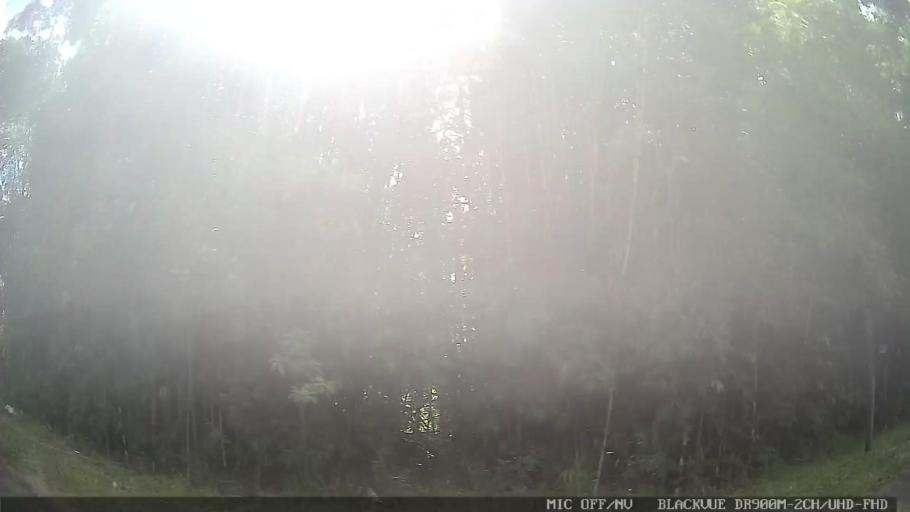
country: BR
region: Sao Paulo
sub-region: Braganca Paulista
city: Braganca Paulista
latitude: -22.8771
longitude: -46.5348
